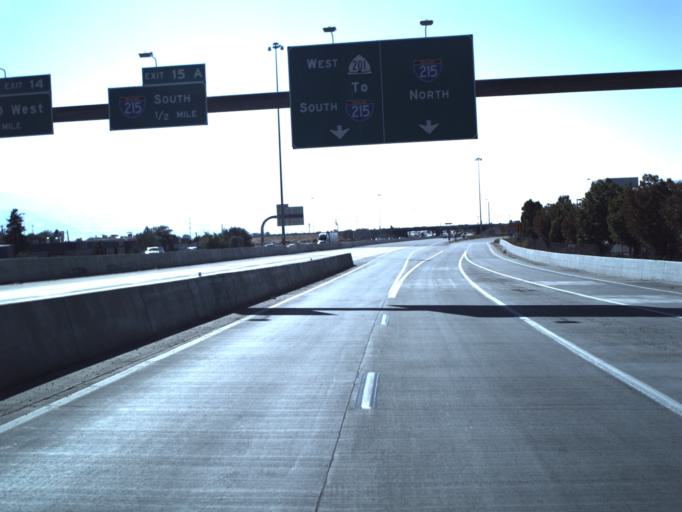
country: US
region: Utah
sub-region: Salt Lake County
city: South Salt Lake
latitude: 40.7243
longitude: -111.9430
